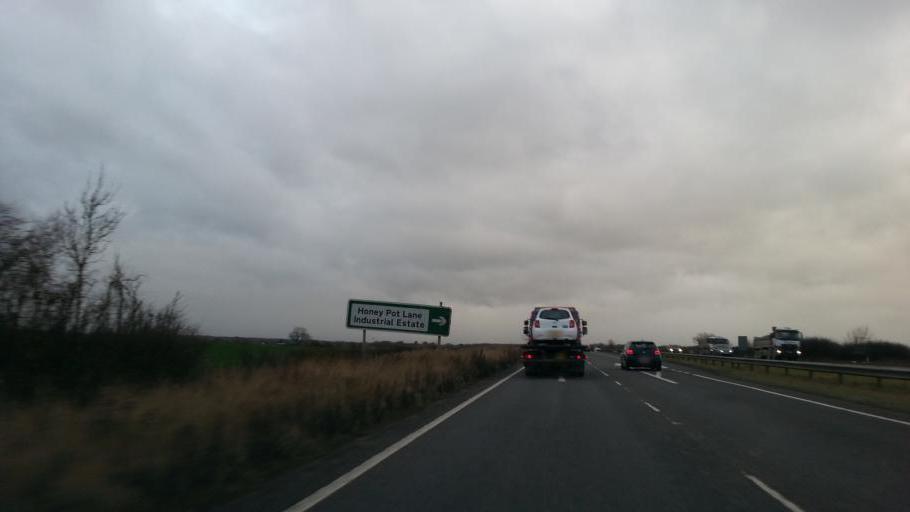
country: GB
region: England
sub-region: District of Rutland
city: Clipsham
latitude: 52.7841
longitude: -0.6111
